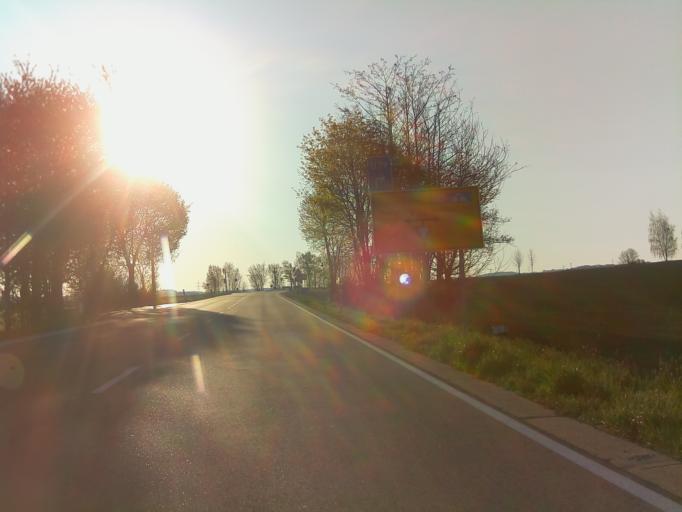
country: DE
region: Baden-Wuerttemberg
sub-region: Regierungsbezirk Stuttgart
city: Kupferzell
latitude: 49.2147
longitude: 9.6731
